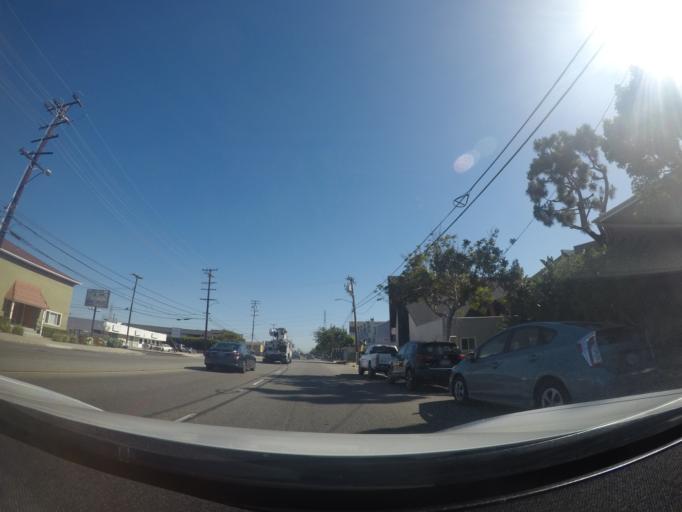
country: US
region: California
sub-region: Los Angeles County
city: Lawndale
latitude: 33.8664
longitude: -118.3437
